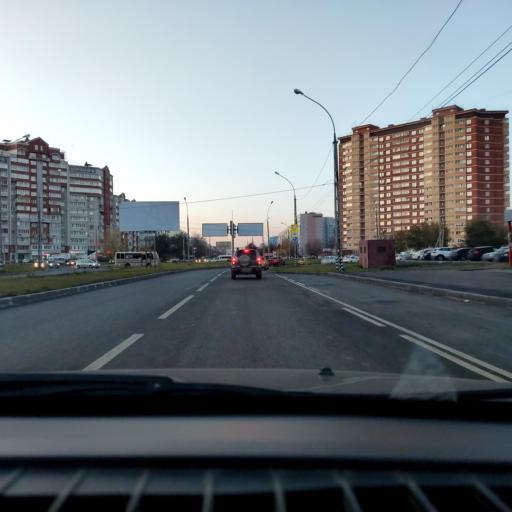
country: RU
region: Samara
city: Tol'yatti
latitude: 53.5435
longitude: 49.3309
